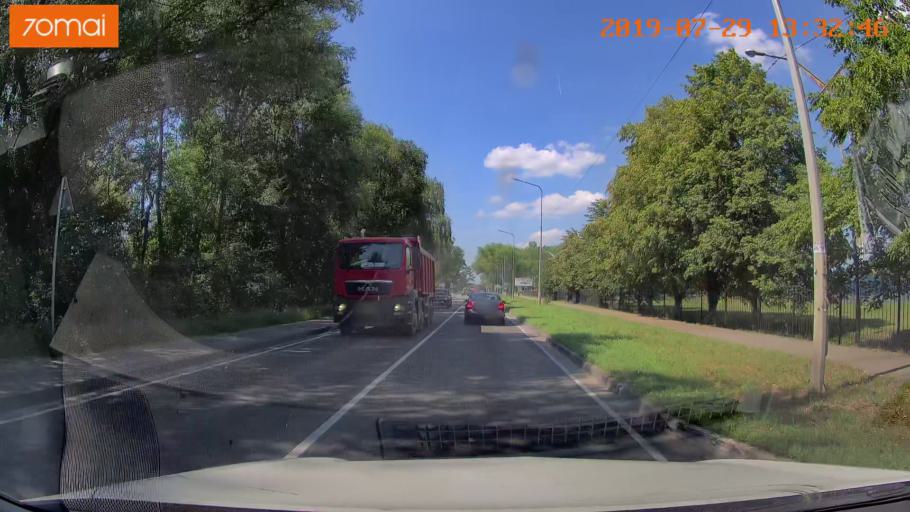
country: RU
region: Kaliningrad
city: Vzmorye
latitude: 54.6980
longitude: 20.2326
